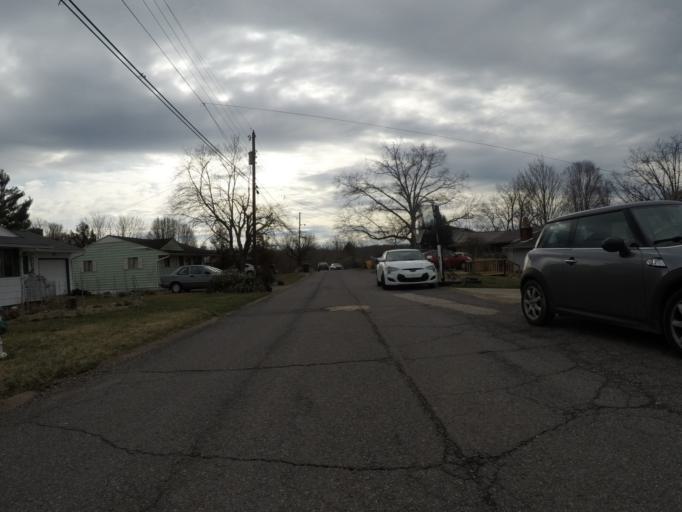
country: US
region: West Virginia
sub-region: Cabell County
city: Pea Ridge
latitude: 38.3932
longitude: -82.3780
